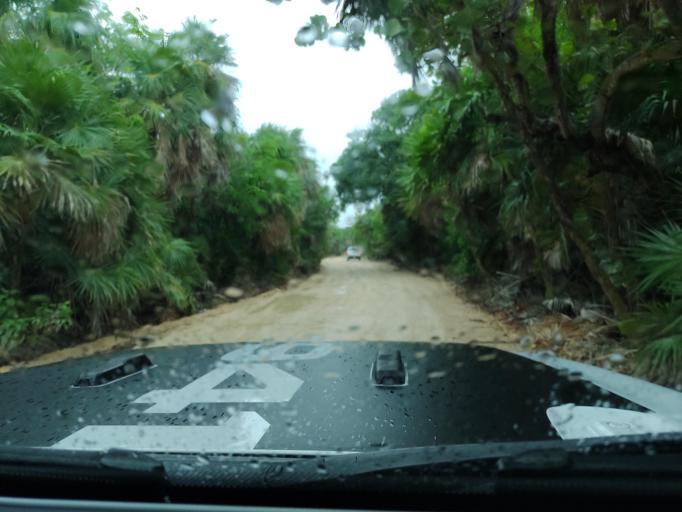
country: MX
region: Quintana Roo
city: Tulum
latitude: 20.0517
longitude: -87.4814
